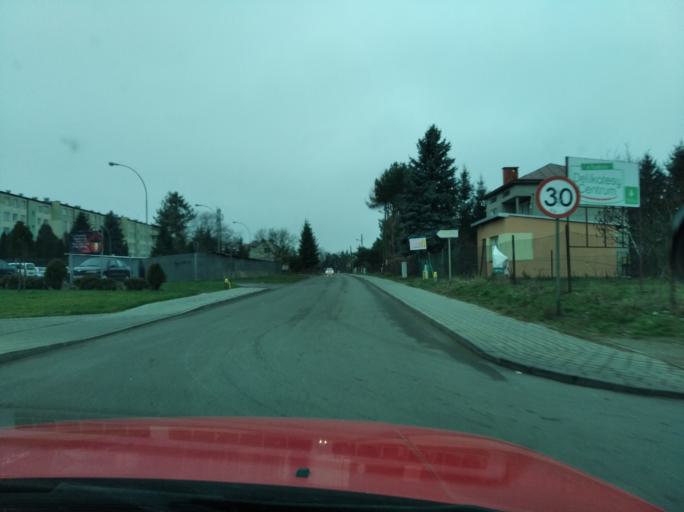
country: PL
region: Subcarpathian Voivodeship
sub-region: Powiat przeworski
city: Przeworsk
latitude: 50.0603
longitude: 22.5074
